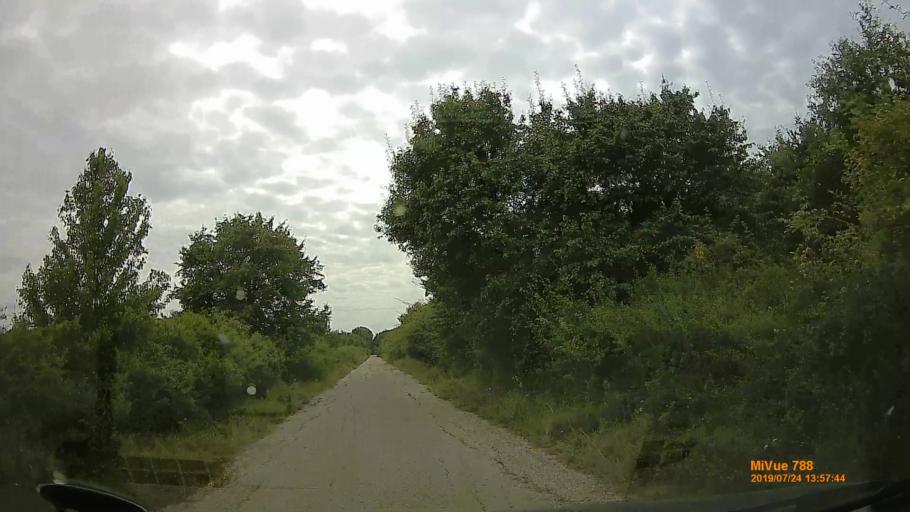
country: HU
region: Szabolcs-Szatmar-Bereg
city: Aranyosapati
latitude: 48.2615
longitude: 22.3283
